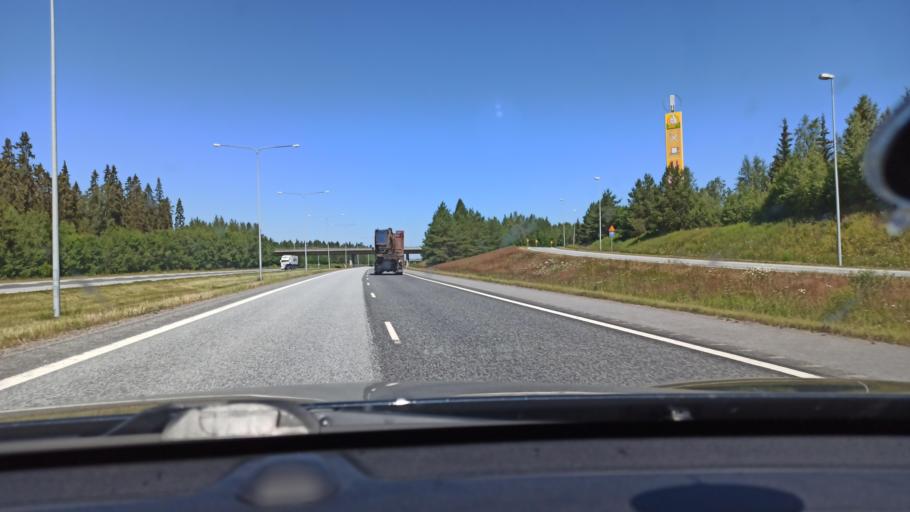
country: FI
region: Ostrobothnia
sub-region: Vaasa
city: Ristinummi
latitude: 63.0519
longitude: 21.7162
